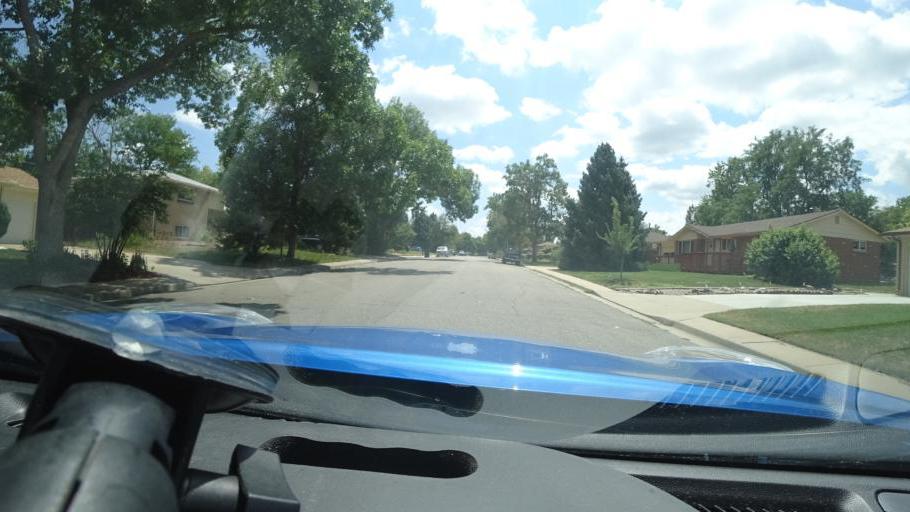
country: US
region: Colorado
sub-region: Adams County
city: Aurora
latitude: 39.7059
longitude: -104.8444
